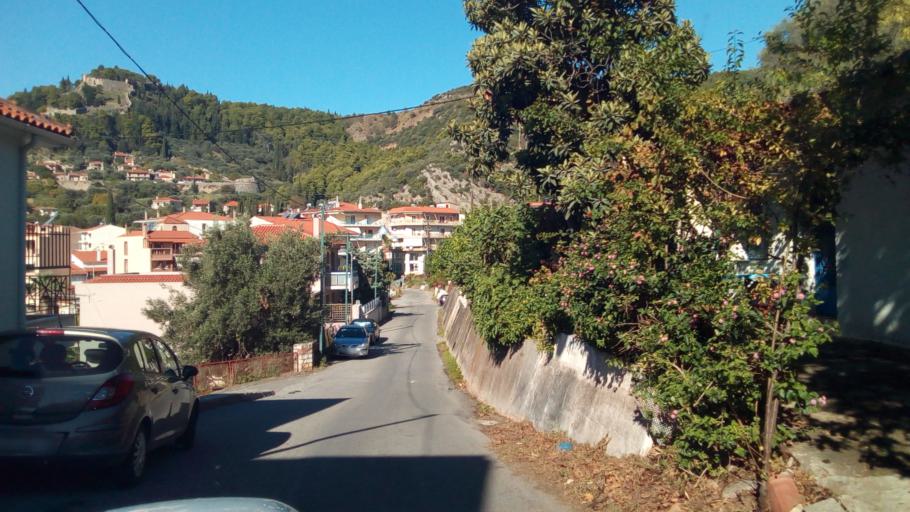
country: GR
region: West Greece
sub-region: Nomos Aitolias kai Akarnanias
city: Nafpaktos
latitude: 38.3964
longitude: 21.8344
